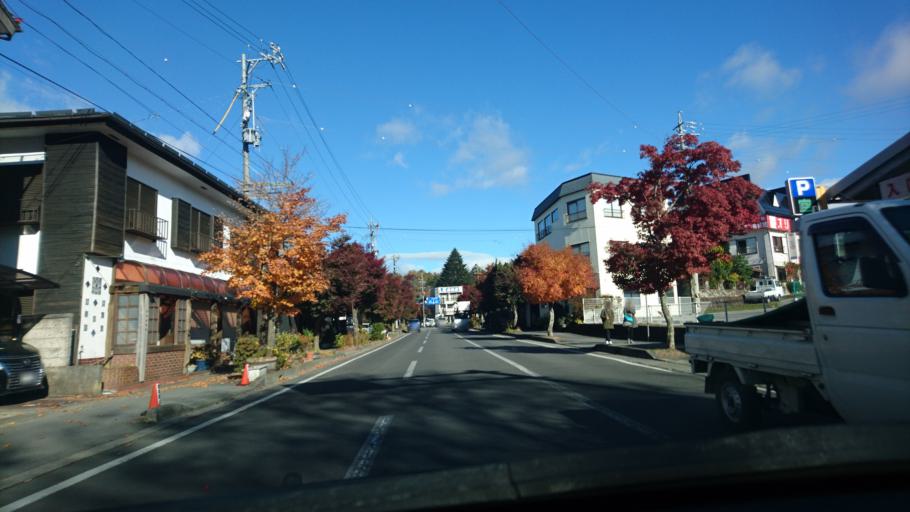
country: JP
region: Nagano
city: Komoro
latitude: 36.3580
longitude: 138.6339
